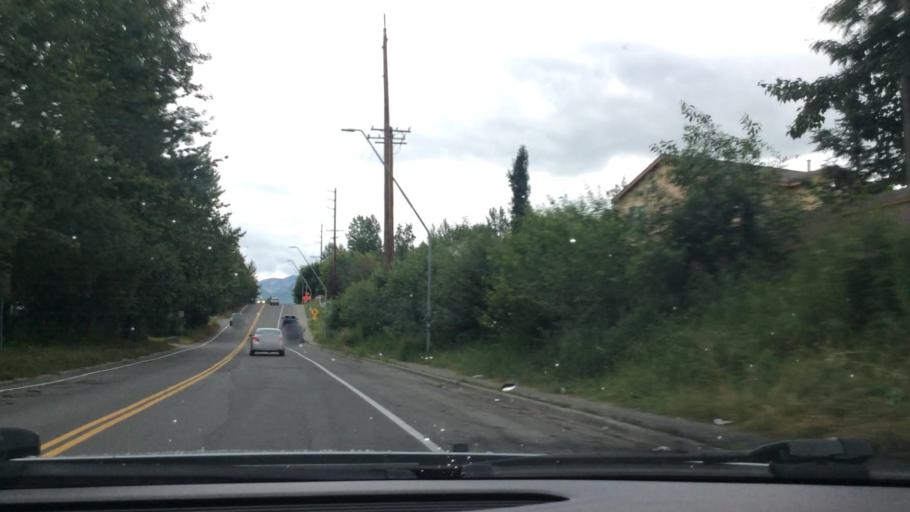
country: US
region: Alaska
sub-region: Anchorage Municipality
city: Elmendorf Air Force Base
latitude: 61.2242
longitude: -149.7411
